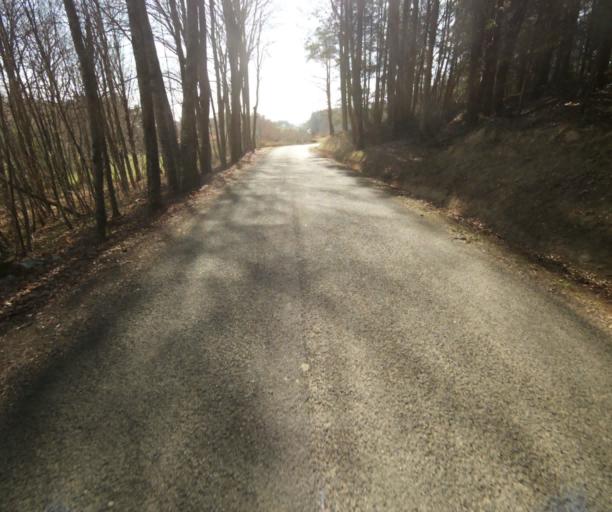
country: FR
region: Limousin
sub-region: Departement de la Correze
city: Saint-Mexant
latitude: 45.3161
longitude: 1.6192
